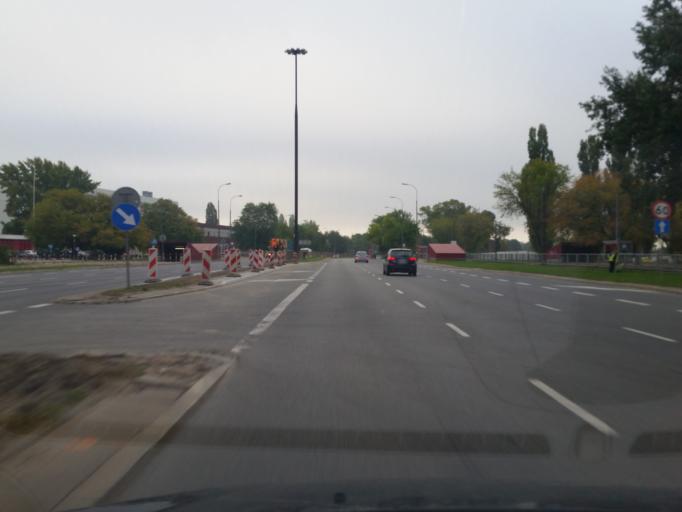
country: PL
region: Masovian Voivodeship
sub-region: Warszawa
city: Zoliborz
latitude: 52.2880
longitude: 21.0053
